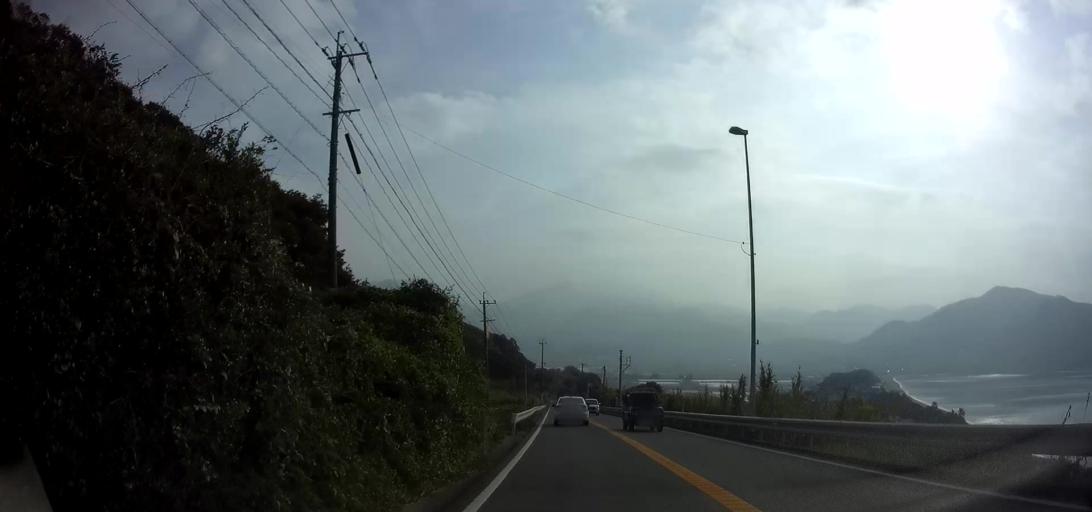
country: JP
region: Nagasaki
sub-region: Isahaya-shi
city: Isahaya
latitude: 32.7953
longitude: 130.1799
